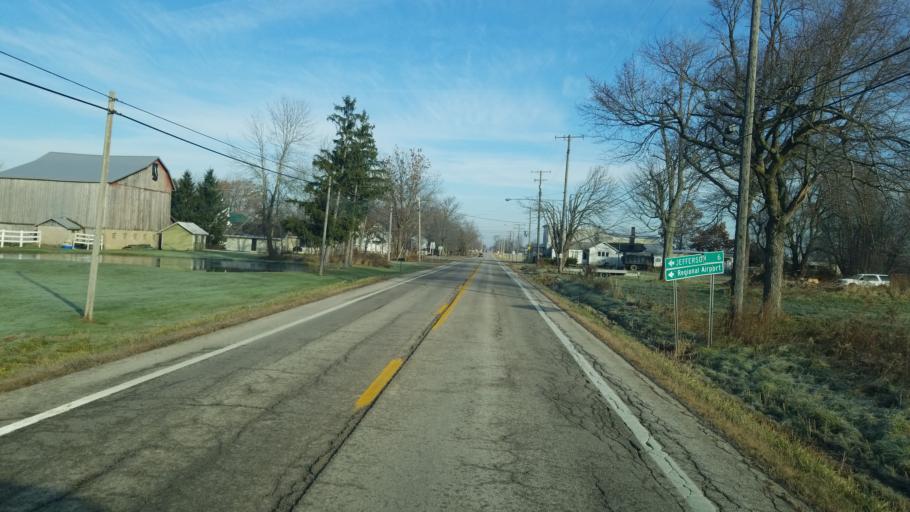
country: US
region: Ohio
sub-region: Ashtabula County
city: Jefferson
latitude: 41.7499
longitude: -80.6676
